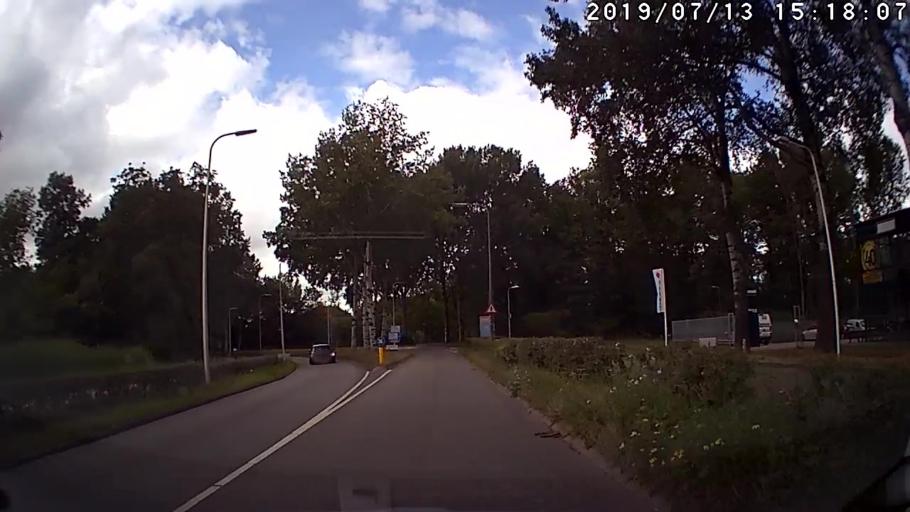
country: NL
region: Overijssel
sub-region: Gemeente Zwolle
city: Zwolle
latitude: 52.5030
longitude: 6.1201
